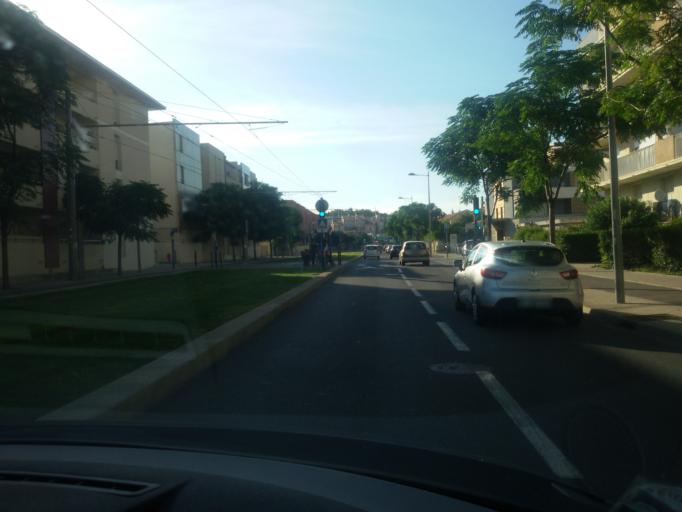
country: FR
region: Languedoc-Roussillon
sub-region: Departement de l'Herault
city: Montpellier
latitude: 43.5913
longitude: 3.8827
